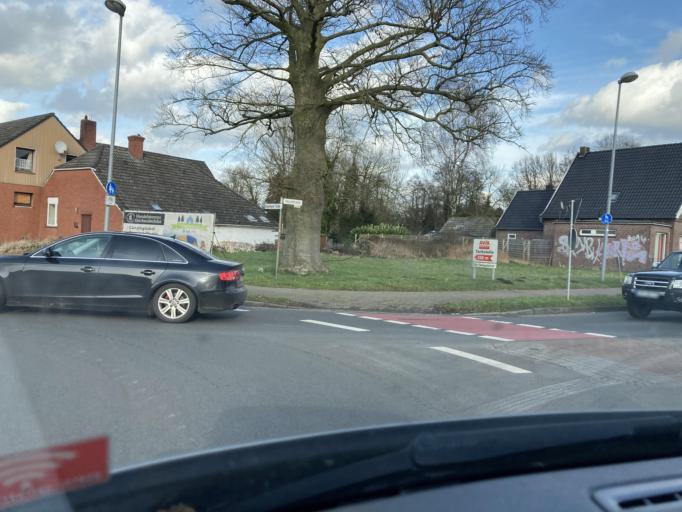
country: DE
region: Lower Saxony
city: Nortmoor
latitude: 53.1593
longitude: 7.5300
